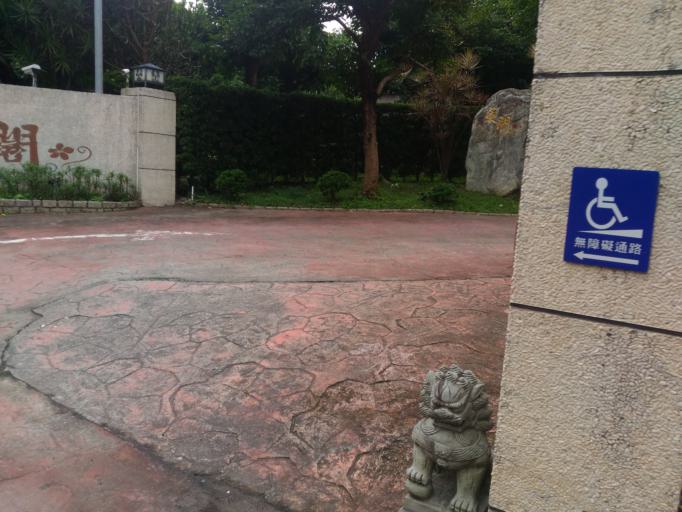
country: TW
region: Taipei
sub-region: Taipei
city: Banqiao
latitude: 24.9640
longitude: 121.4384
